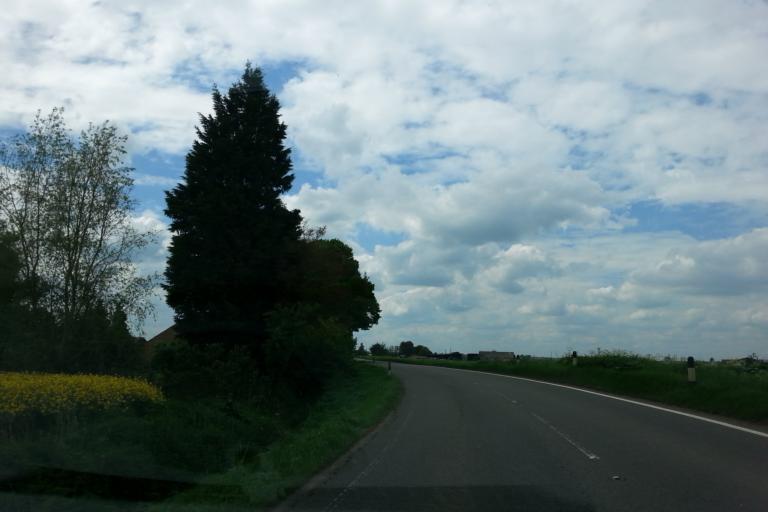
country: GB
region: England
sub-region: Cambridgeshire
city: Ramsey
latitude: 52.4675
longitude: -0.1300
